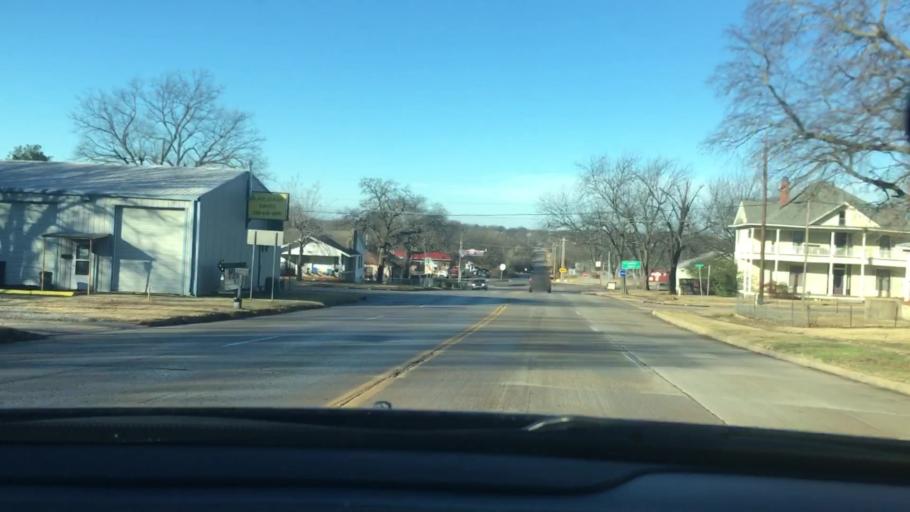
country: US
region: Oklahoma
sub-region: Murray County
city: Sulphur
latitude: 34.5110
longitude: -96.9666
